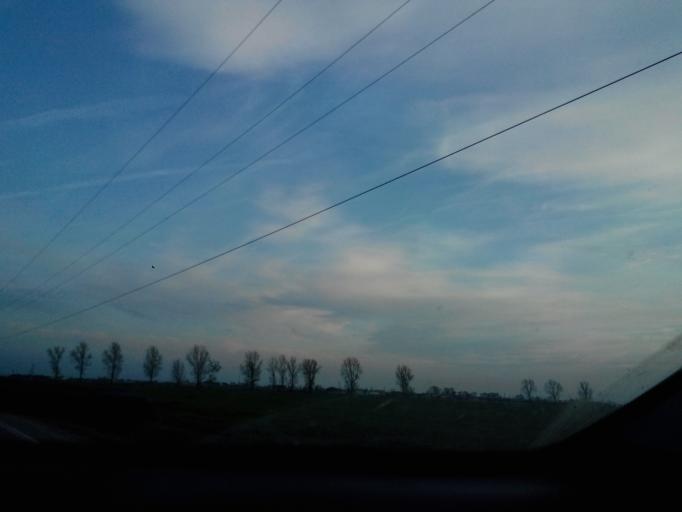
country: RO
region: Prahova
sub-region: Comuna Floresti
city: Floresti
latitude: 45.0470
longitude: 25.8064
